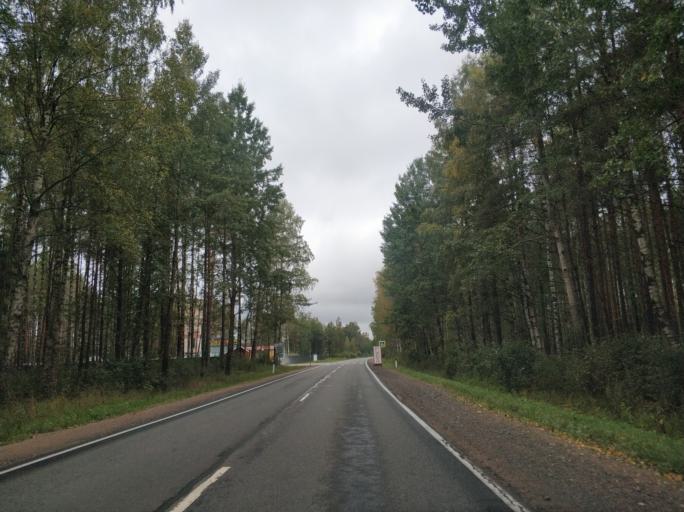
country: RU
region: Leningrad
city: Borisova Griva
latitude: 60.0915
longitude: 30.8569
